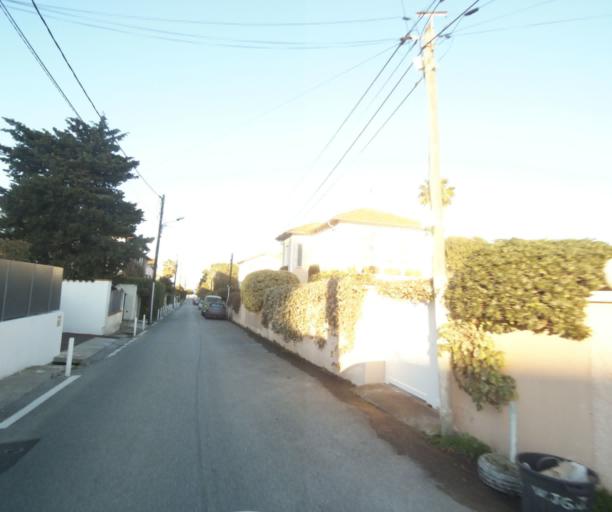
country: FR
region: Provence-Alpes-Cote d'Azur
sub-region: Departement des Alpes-Maritimes
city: Antibes
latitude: 43.5670
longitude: 7.1287
